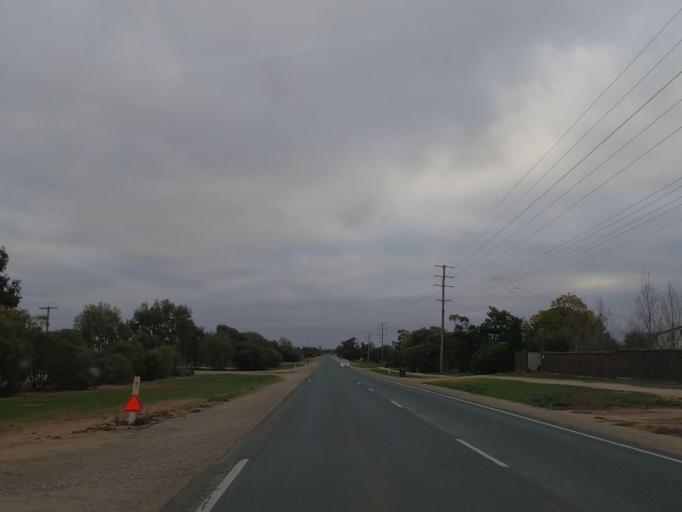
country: AU
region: Victoria
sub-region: Swan Hill
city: Swan Hill
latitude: -35.4669
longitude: 143.6497
